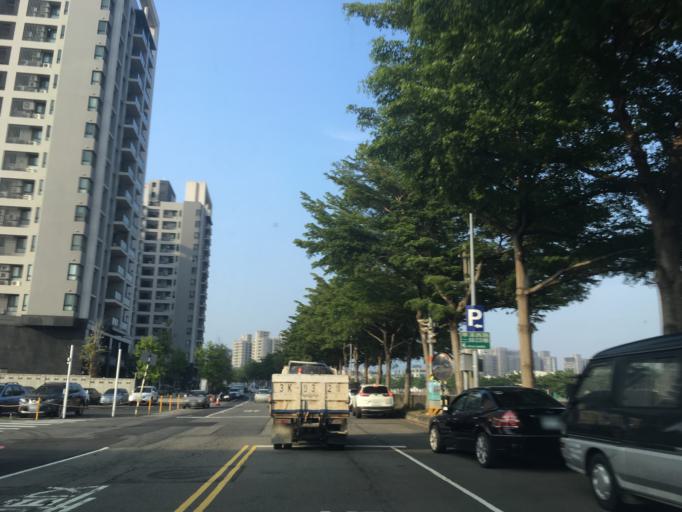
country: TW
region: Taiwan
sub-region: Taichung City
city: Taichung
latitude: 24.1550
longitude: 120.7028
